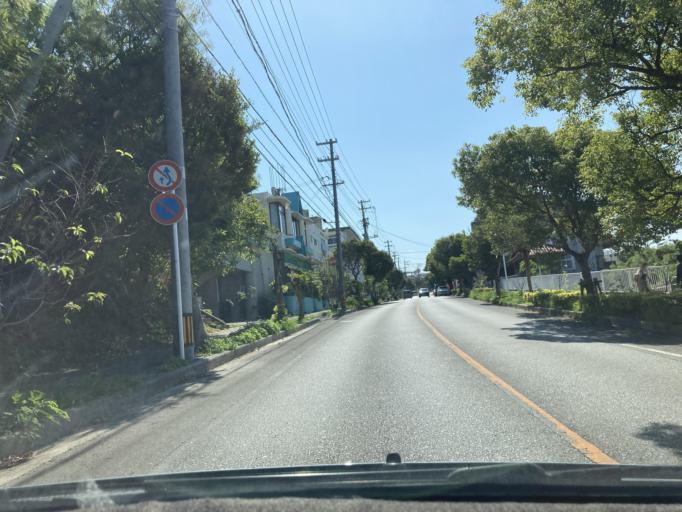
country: JP
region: Okinawa
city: Ginowan
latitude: 26.2520
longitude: 127.7258
